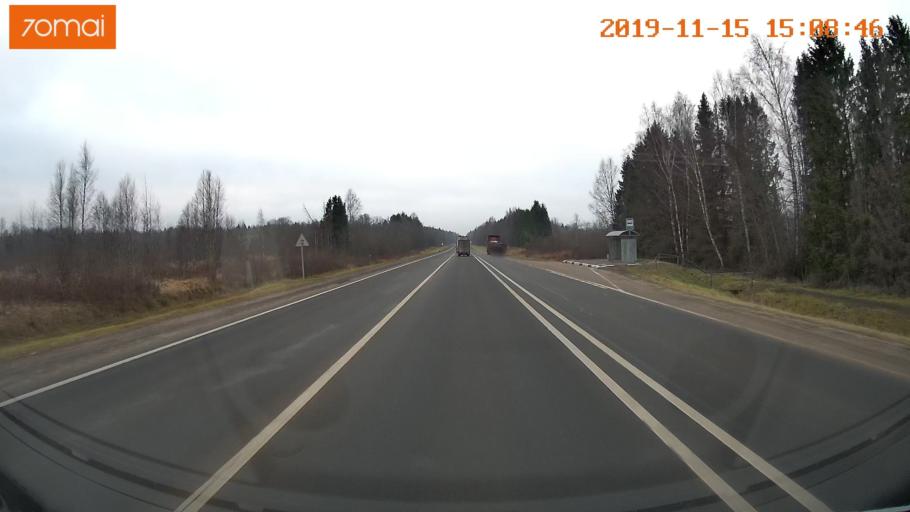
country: RU
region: Jaroslavl
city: Prechistoye
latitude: 58.3662
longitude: 40.2724
